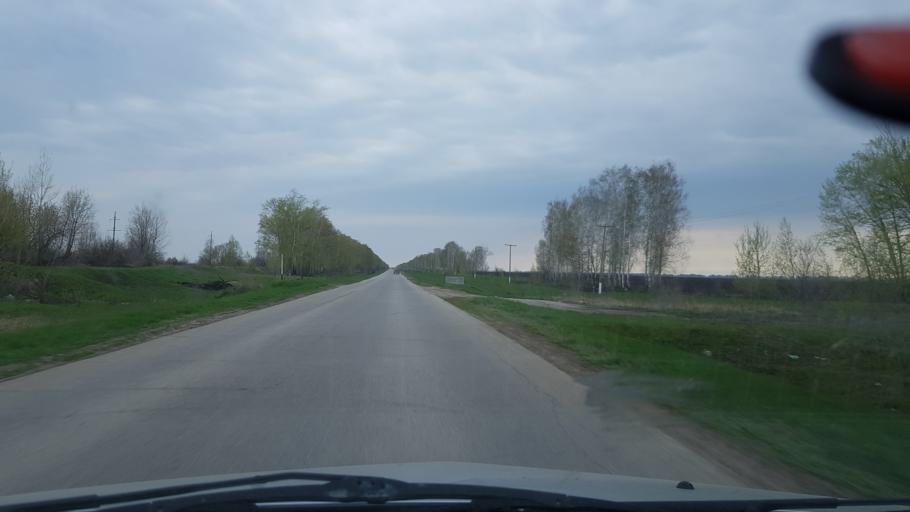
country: RU
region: Samara
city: Tol'yatti
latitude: 53.6583
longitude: 49.2415
